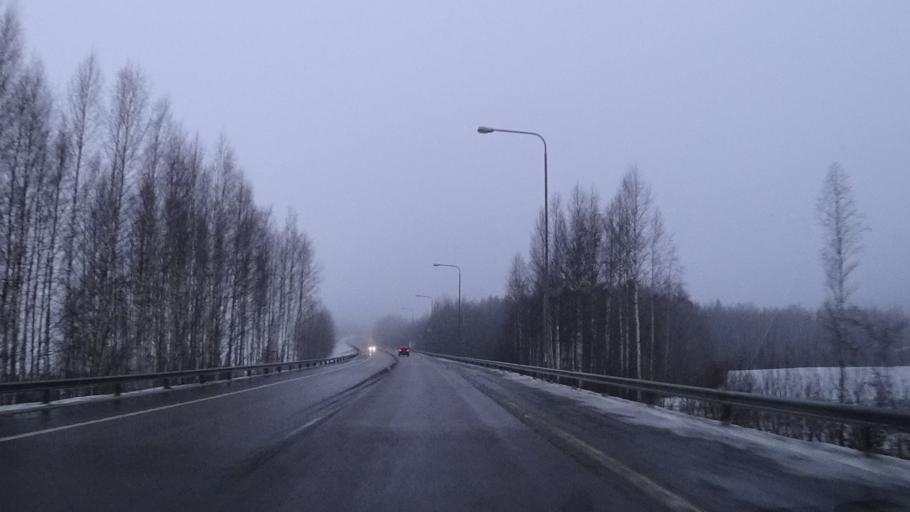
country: FI
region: Paijanne Tavastia
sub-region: Lahti
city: Hollola
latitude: 60.9838
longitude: 25.4457
